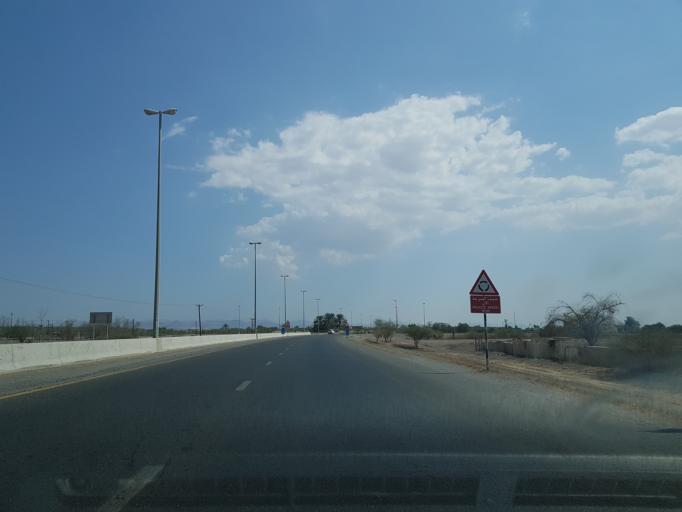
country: AE
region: Ash Shariqah
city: Adh Dhayd
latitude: 25.2447
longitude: 55.9123
